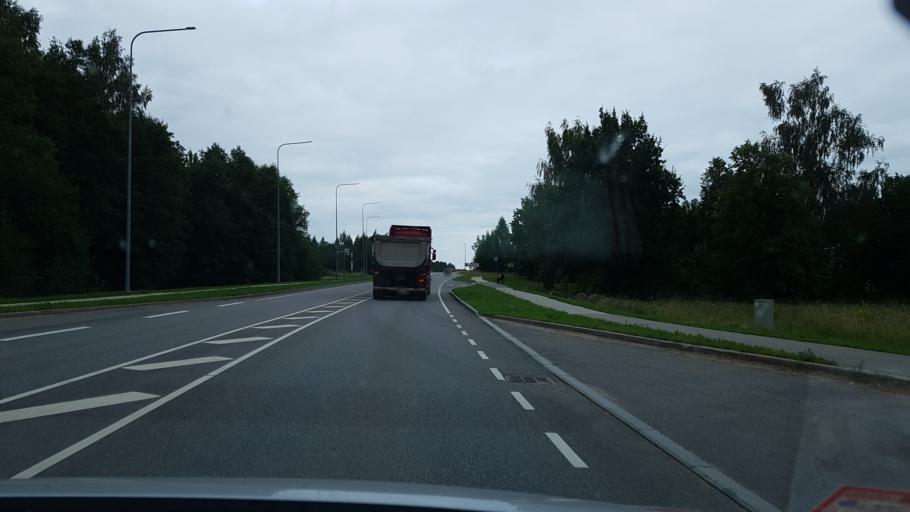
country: EE
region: Tartu
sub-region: UElenurme vald
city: Ulenurme
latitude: 58.3317
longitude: 26.9786
